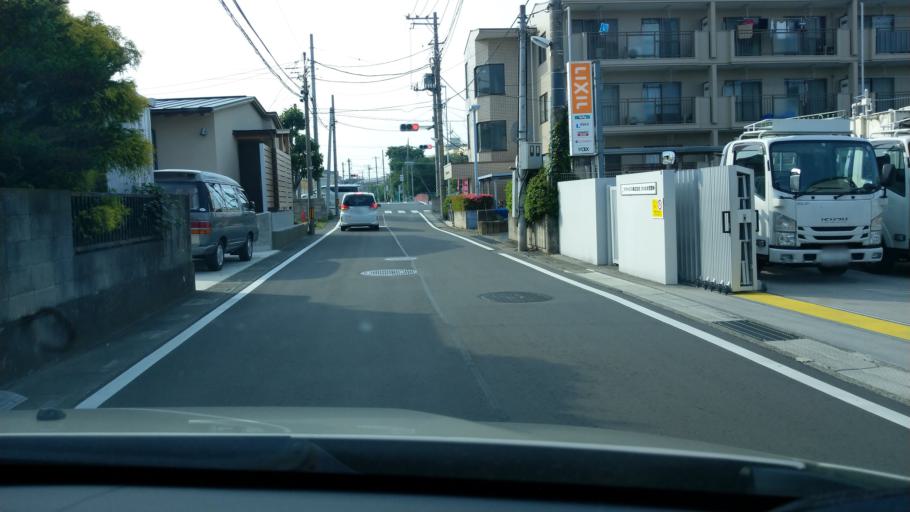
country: JP
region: Saitama
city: Yono
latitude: 35.8948
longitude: 139.6176
